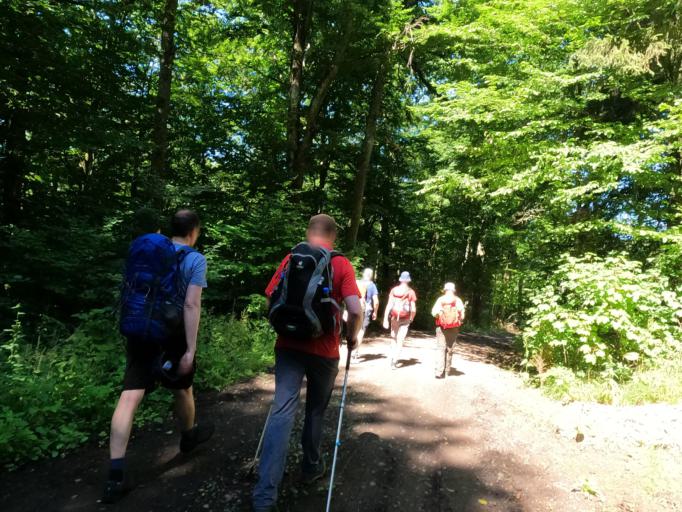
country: DE
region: Bavaria
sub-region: Regierungsbezirk Unterfranken
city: Zeitlofs
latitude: 50.3327
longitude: 9.6344
